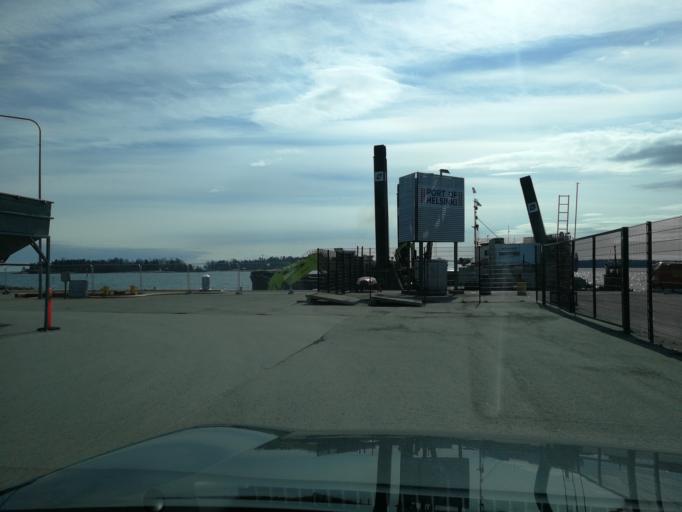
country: FI
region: Uusimaa
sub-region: Helsinki
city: Helsinki
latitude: 60.1485
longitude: 24.9202
